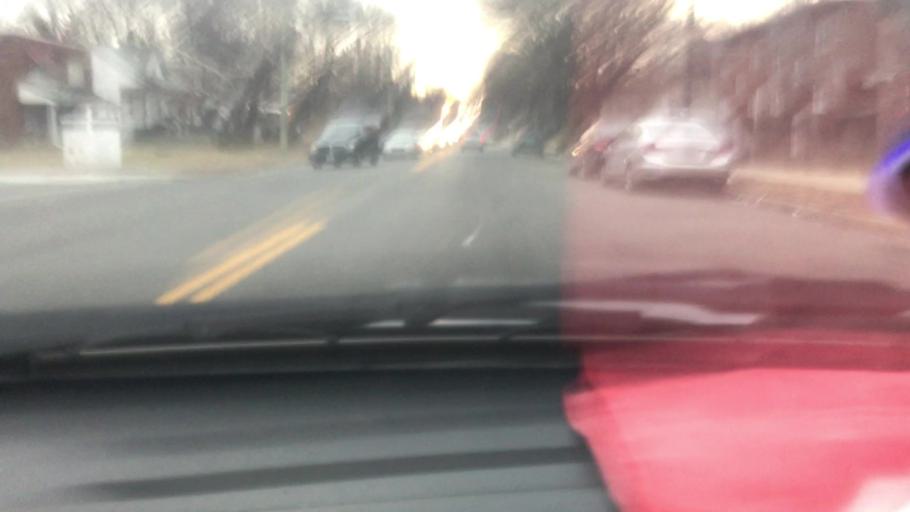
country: US
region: Maryland
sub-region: Prince George's County
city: Fairmount Heights
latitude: 38.9095
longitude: -76.9306
